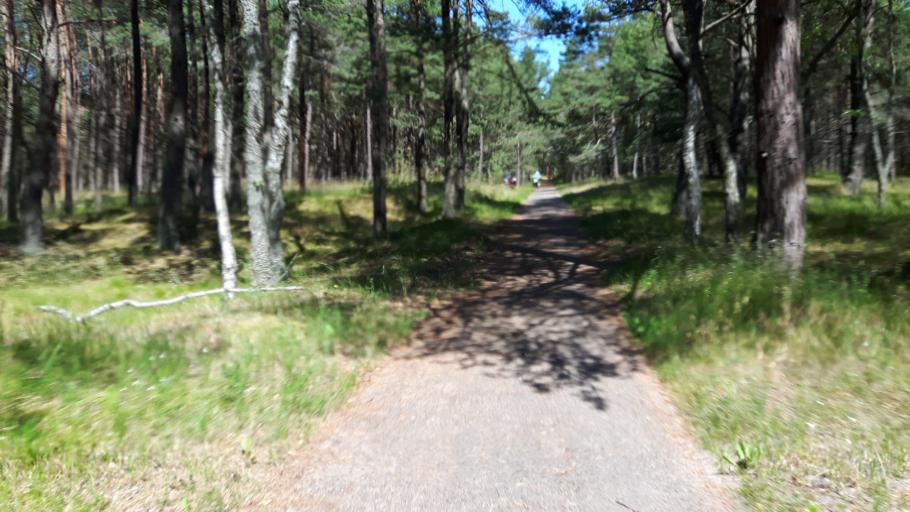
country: LT
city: Neringa
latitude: 55.4245
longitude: 21.0758
